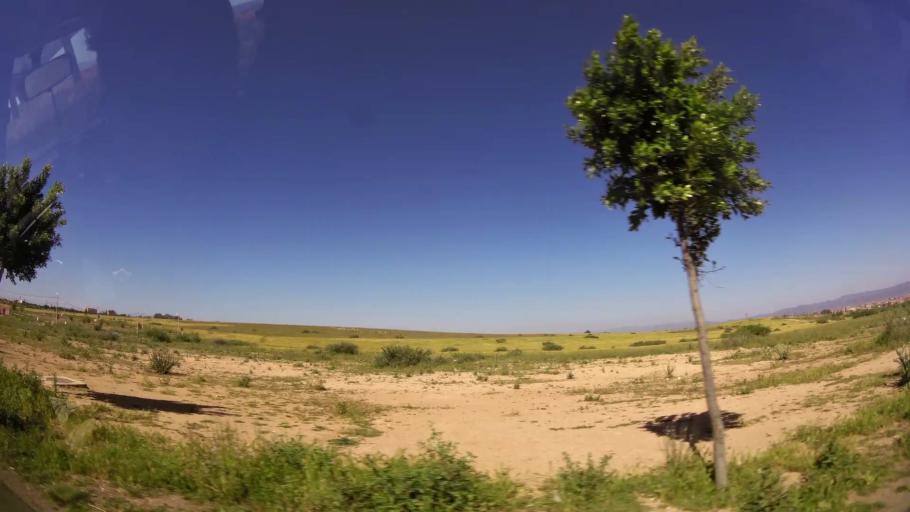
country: MA
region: Oriental
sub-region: Oujda-Angad
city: Oujda
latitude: 34.7318
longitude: -1.9173
